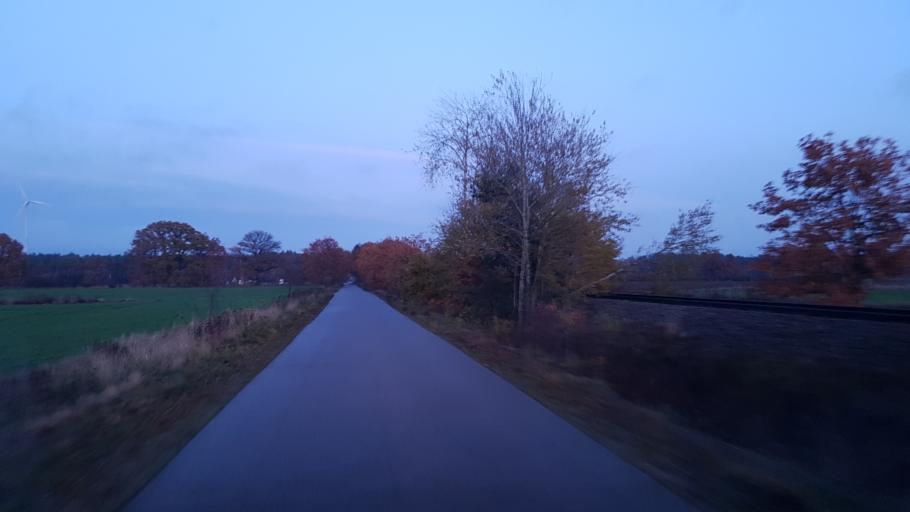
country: DE
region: Brandenburg
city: Falkenberg
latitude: 51.6241
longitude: 13.2134
